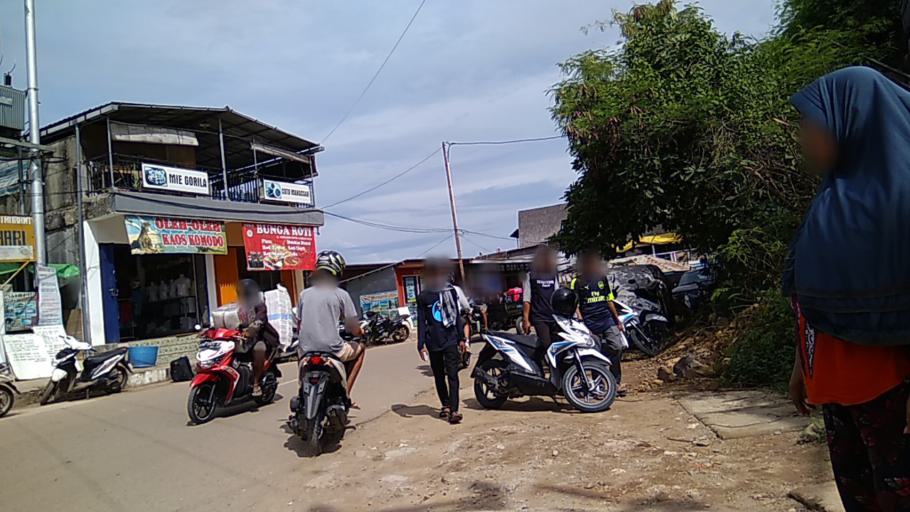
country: ID
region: East Nusa Tenggara
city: Cempa
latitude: -8.4960
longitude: 119.8789
